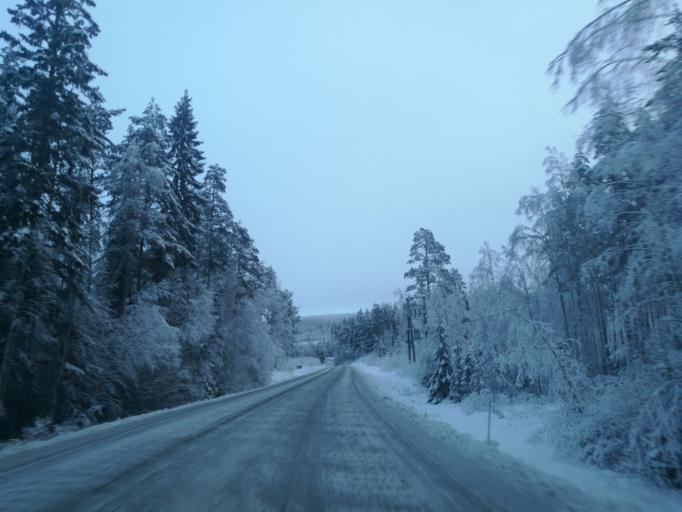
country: NO
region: Hedmark
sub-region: Grue
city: Kirkenaer
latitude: 60.3194
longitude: 12.2762
